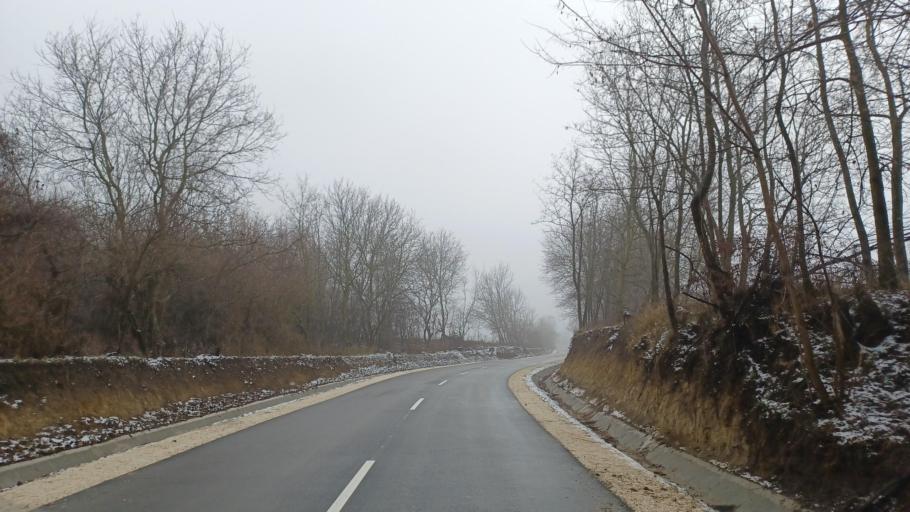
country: HU
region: Tolna
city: Gyonk
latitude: 46.5992
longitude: 18.4737
